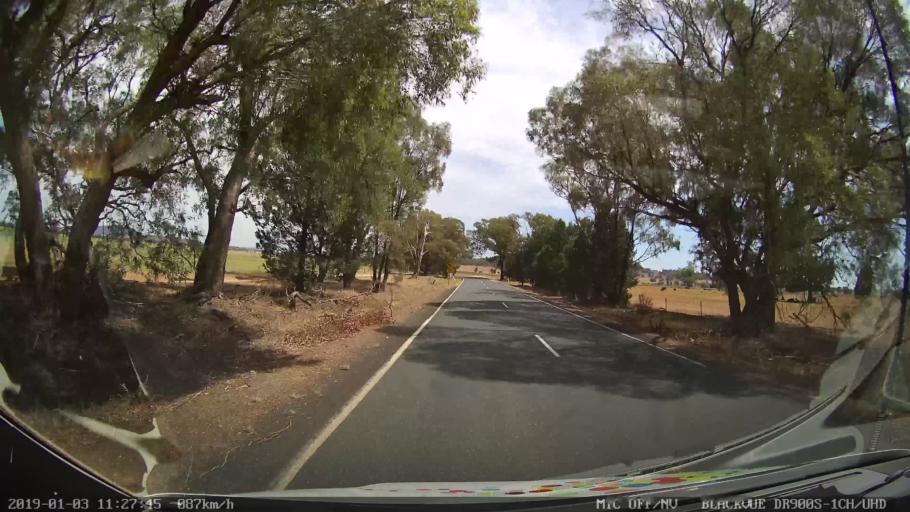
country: AU
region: New South Wales
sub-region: Weddin
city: Grenfell
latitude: -34.0089
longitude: 148.2164
